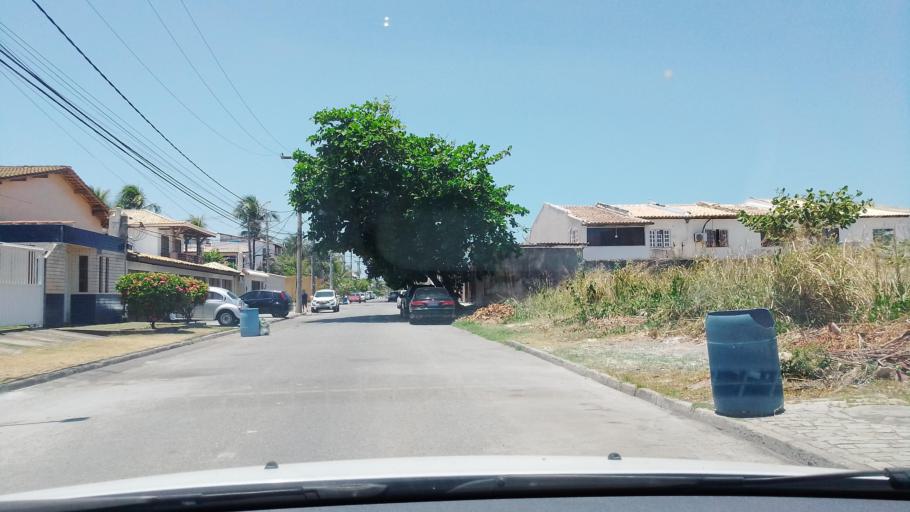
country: BR
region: Bahia
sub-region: Lauro De Freitas
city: Lauro de Freitas
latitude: -12.9406
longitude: -38.3327
